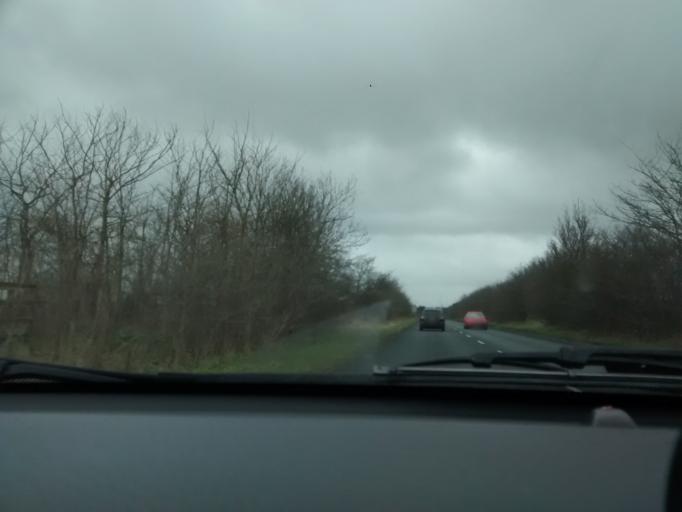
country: GB
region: England
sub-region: Suffolk
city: Felixstowe
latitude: 51.9762
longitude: 1.3380
